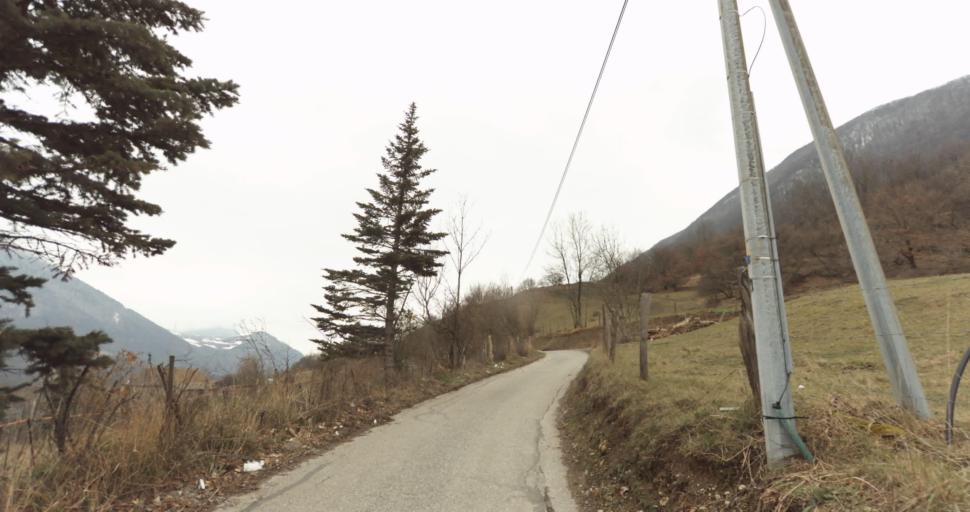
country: FR
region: Rhone-Alpes
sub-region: Departement de l'Isere
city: Saint-Georges-de-Commiers
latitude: 45.0241
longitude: 5.6891
